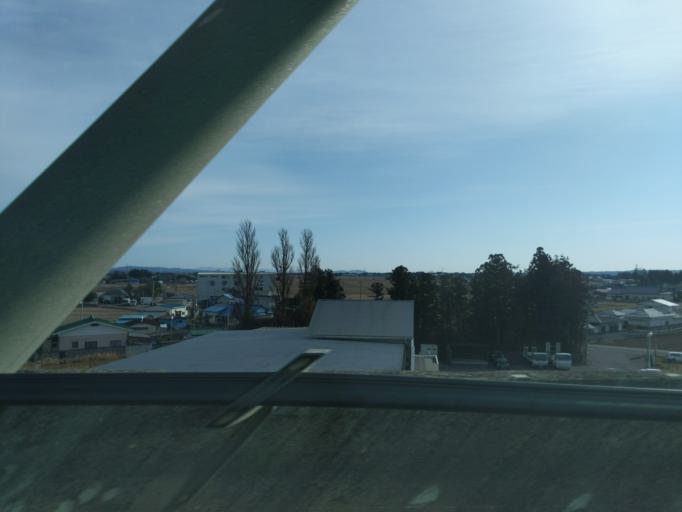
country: JP
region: Miyagi
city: Furukawa
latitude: 38.5913
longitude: 140.9762
